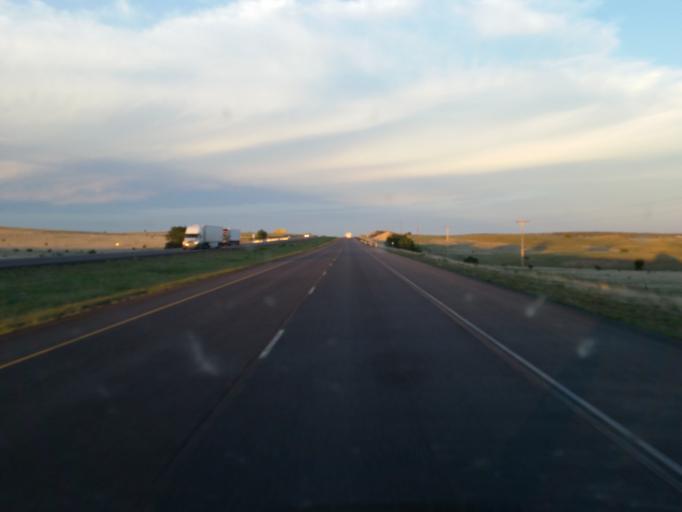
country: US
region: New Mexico
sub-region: Guadalupe County
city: Santa Rosa
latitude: 34.9907
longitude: -105.2804
